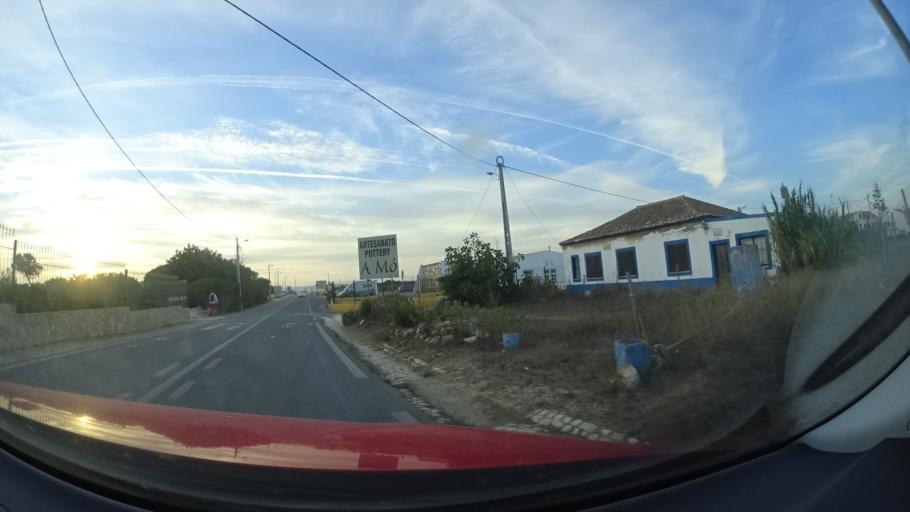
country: PT
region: Faro
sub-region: Vila do Bispo
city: Sagres
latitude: 37.0080
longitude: -8.9461
